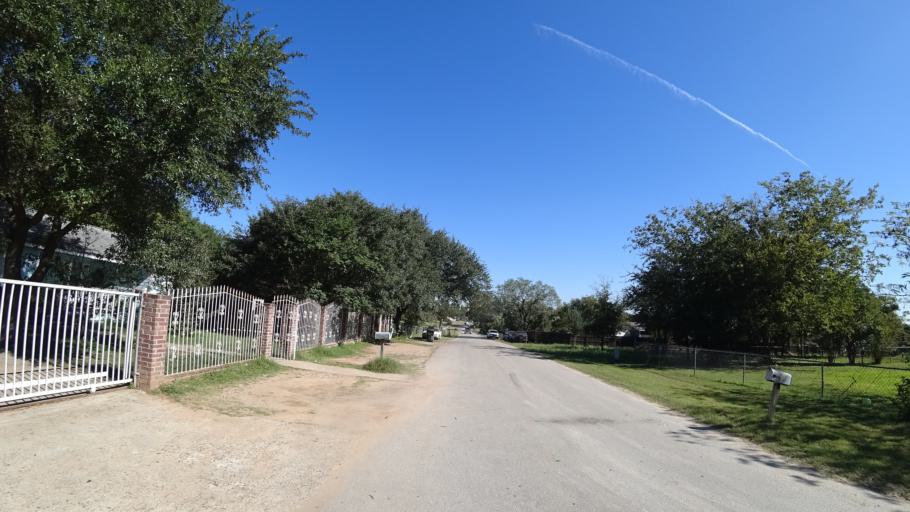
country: US
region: Texas
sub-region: Travis County
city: Hornsby Bend
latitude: 30.2630
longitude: -97.6273
